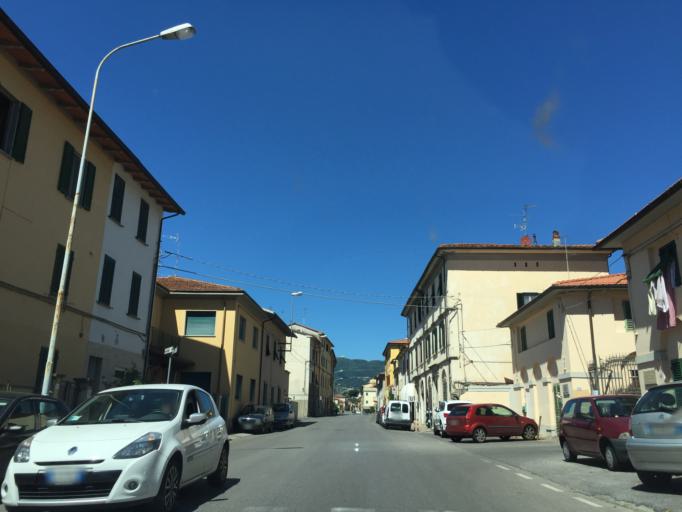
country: IT
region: Tuscany
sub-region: Provincia di Pistoia
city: Pistoia
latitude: 43.9495
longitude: 10.9041
